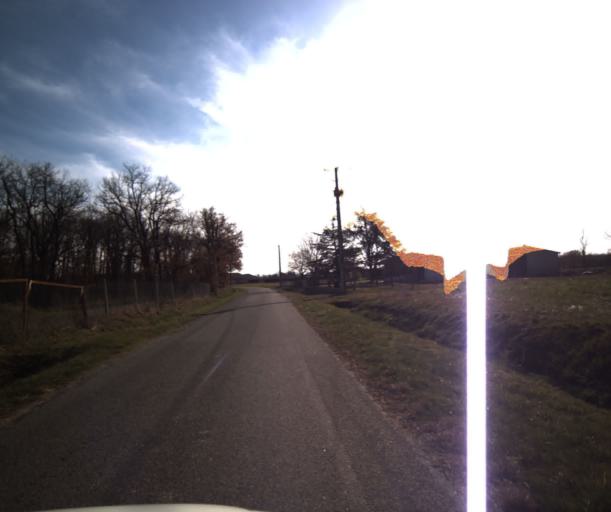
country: FR
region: Midi-Pyrenees
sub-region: Departement du Tarn-et-Garonne
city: Campsas
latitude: 43.9200
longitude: 1.3274
